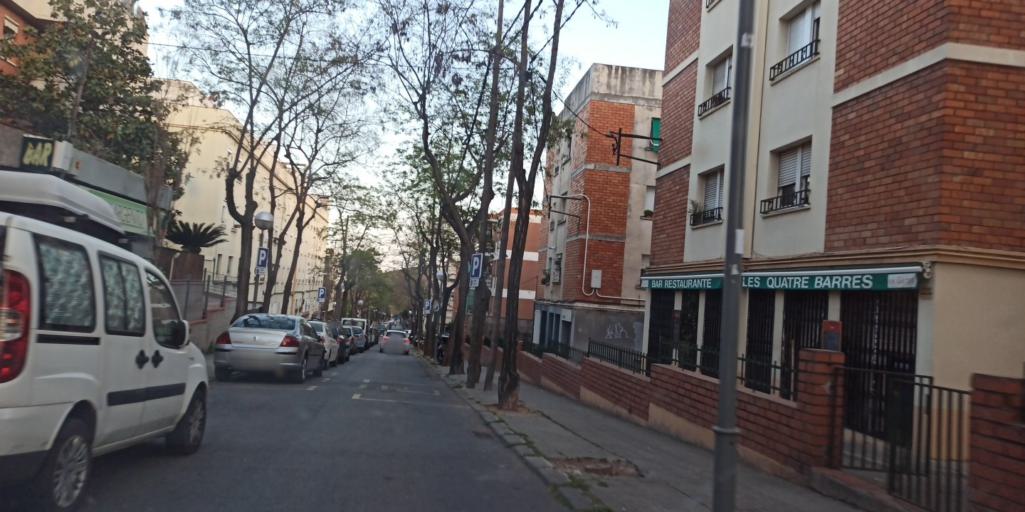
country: ES
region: Catalonia
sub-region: Provincia de Barcelona
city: Nou Barris
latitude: 41.4378
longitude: 2.1579
